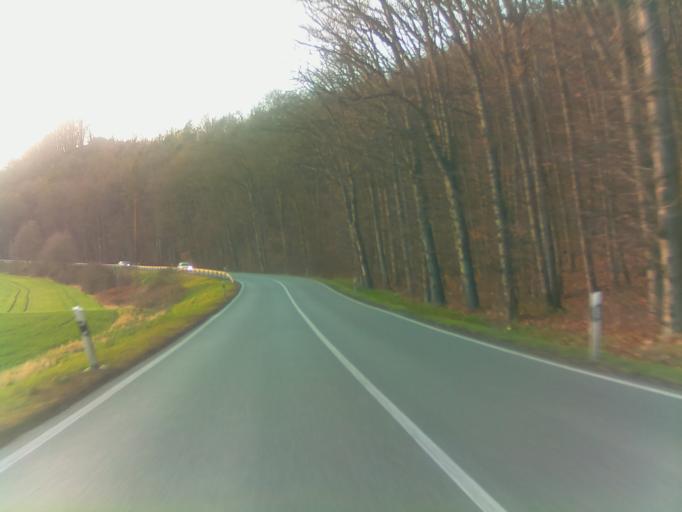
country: DE
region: Thuringia
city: Reinstadt
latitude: 50.7371
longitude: 11.4268
